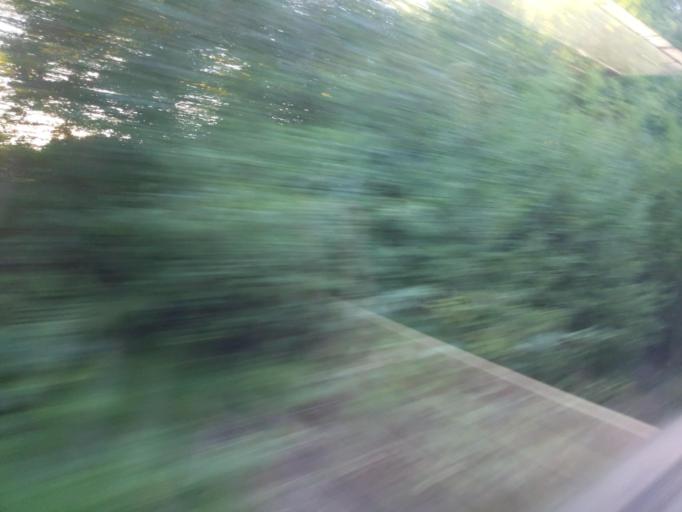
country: GB
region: England
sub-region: Devon
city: Kingskerswell
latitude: 50.5063
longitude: -3.5870
